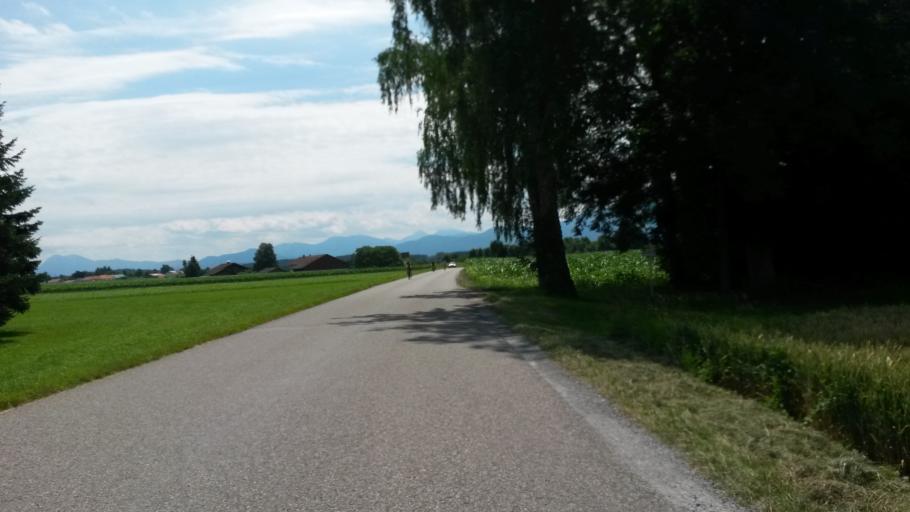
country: DE
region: Bavaria
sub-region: Upper Bavaria
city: Chieming
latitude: 47.9022
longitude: 12.5265
